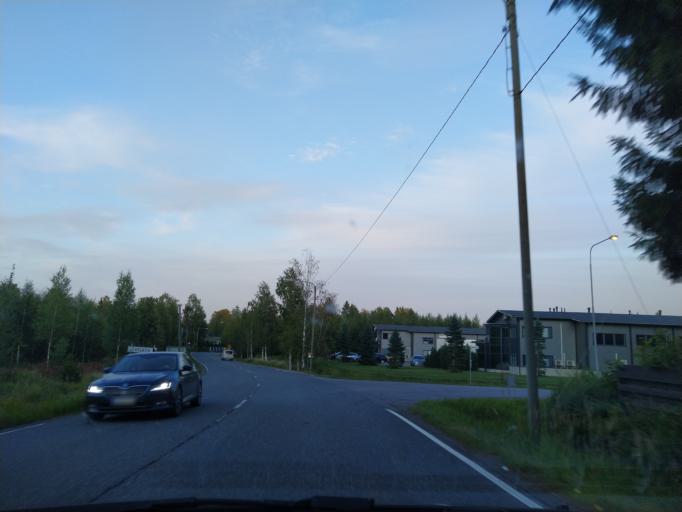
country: FI
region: Uusimaa
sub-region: Helsinki
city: Tuusula
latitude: 60.3543
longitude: 25.0373
